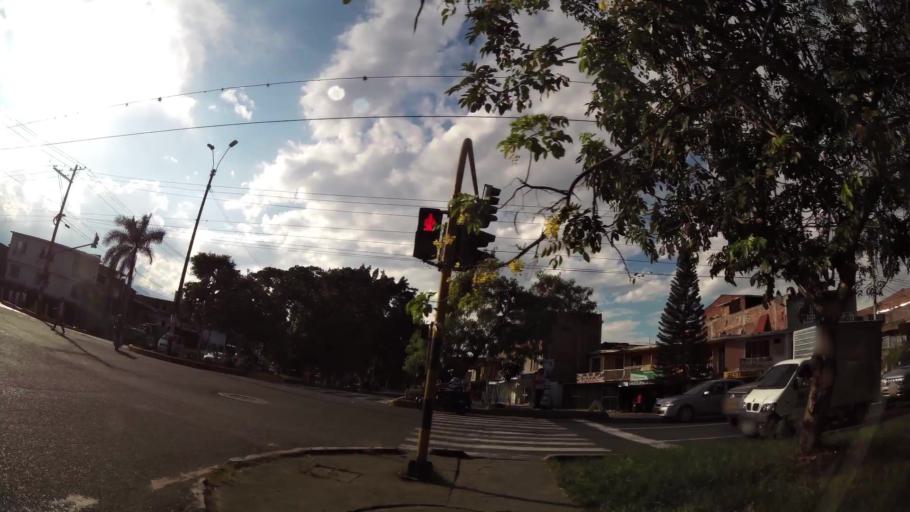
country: CO
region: Valle del Cauca
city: Cali
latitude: 3.4050
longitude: -76.5010
